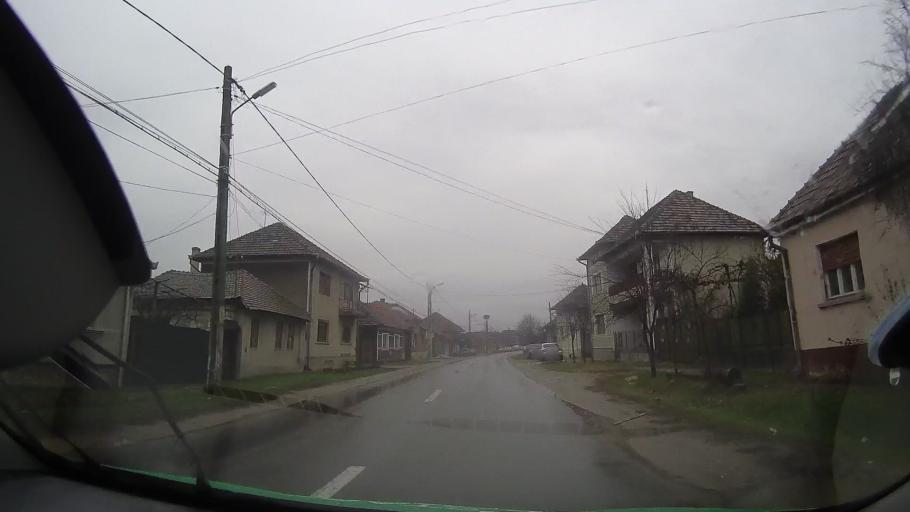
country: RO
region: Bihor
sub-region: Comuna Tinca
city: Tinca
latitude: 46.7721
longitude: 21.9243
